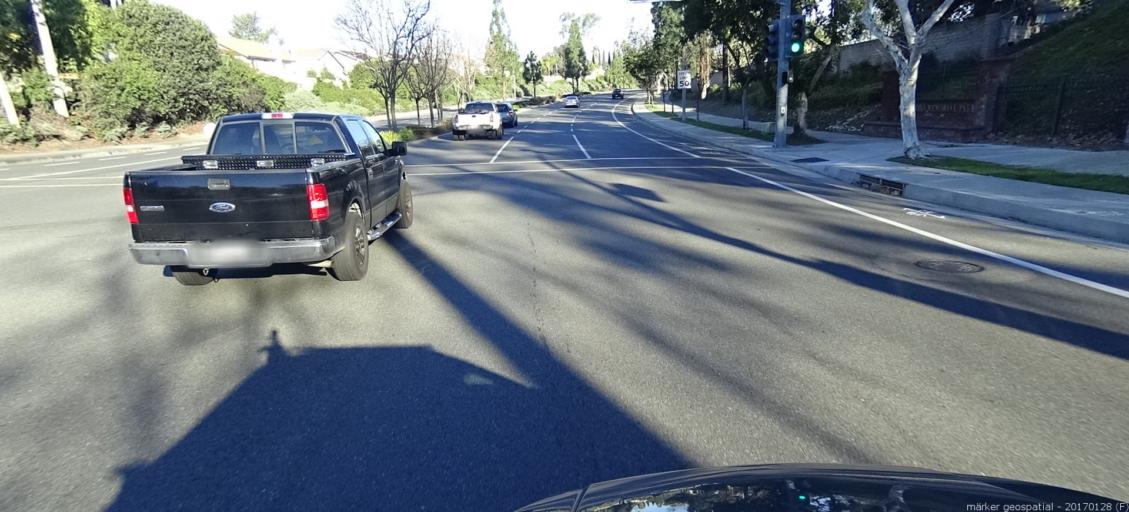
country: US
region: California
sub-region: Orange County
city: Lake Forest
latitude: 33.6417
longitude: -117.6840
